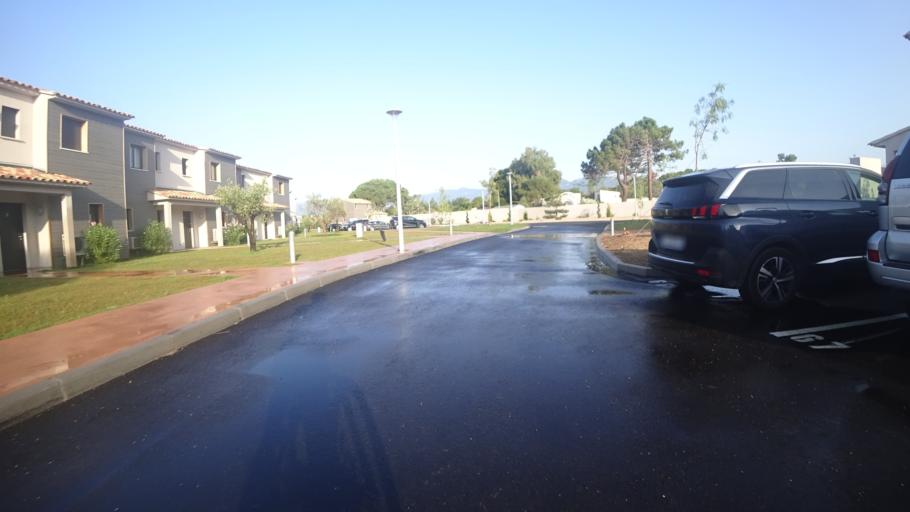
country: FR
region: Corsica
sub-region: Departement de la Corse-du-Sud
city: Porto-Vecchio
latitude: 41.6286
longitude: 9.3360
